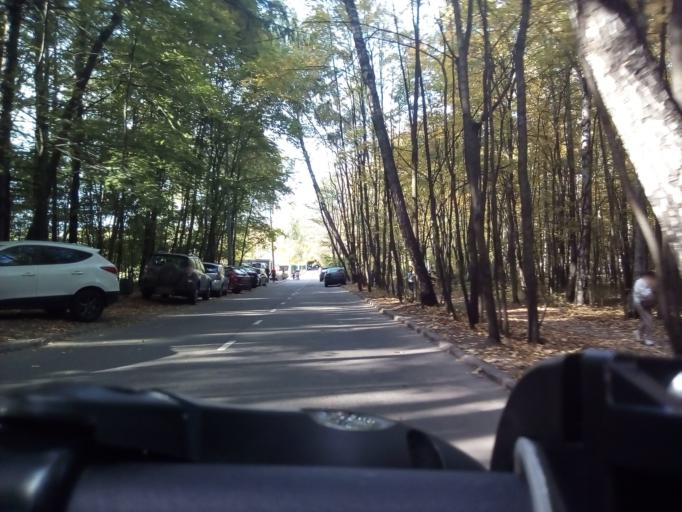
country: RU
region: Moscow
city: Sokol'niki
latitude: 55.8094
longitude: 37.6667
